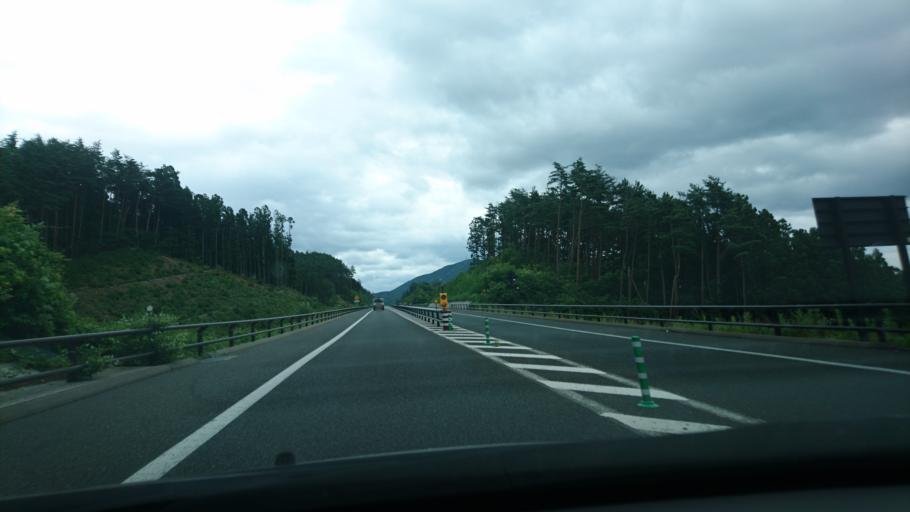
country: JP
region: Iwate
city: Ofunato
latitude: 39.0300
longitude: 141.6483
